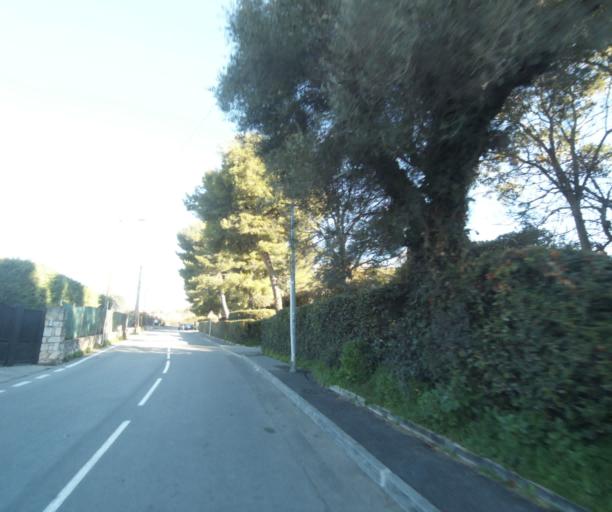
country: FR
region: Provence-Alpes-Cote d'Azur
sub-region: Departement des Alpes-Maritimes
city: Antibes
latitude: 43.5803
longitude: 7.0944
